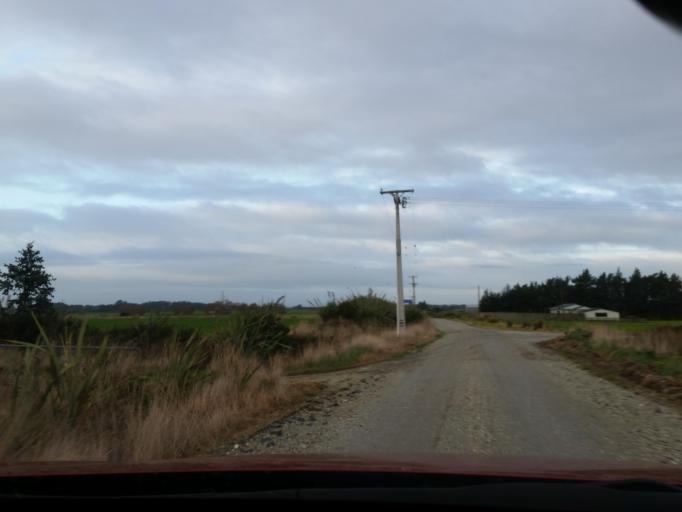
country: NZ
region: Southland
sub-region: Invercargill City
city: Bluff
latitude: -46.5324
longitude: 168.5690
